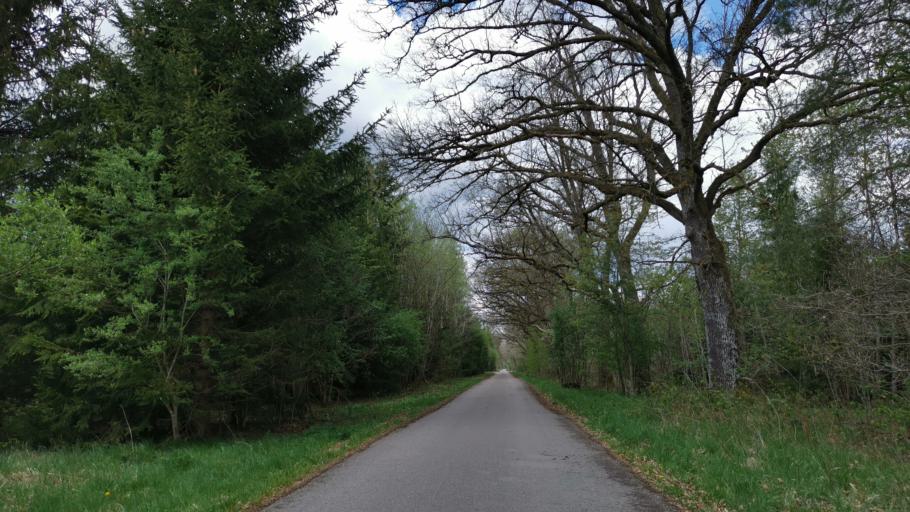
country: DE
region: Bavaria
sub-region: Upper Bavaria
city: Neuried
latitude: 48.0563
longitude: 11.4554
